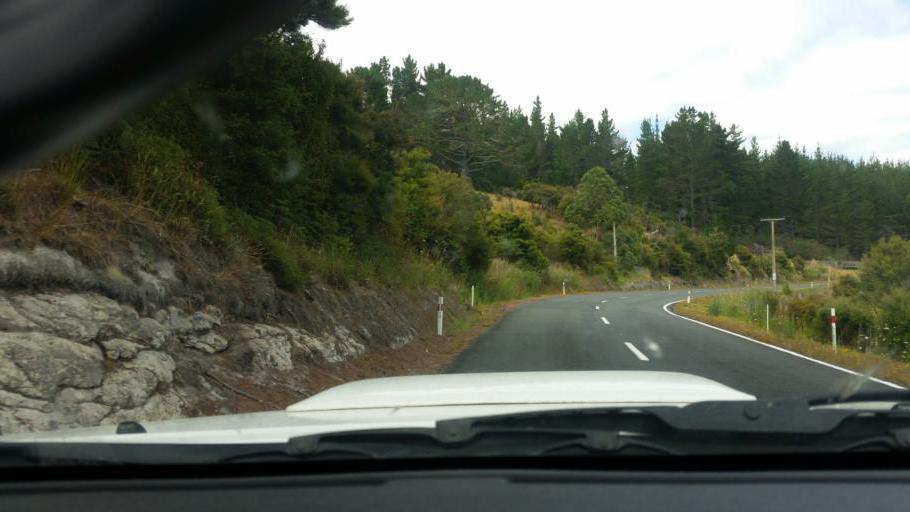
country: NZ
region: Northland
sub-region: Kaipara District
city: Dargaville
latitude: -35.8155
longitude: 173.7264
